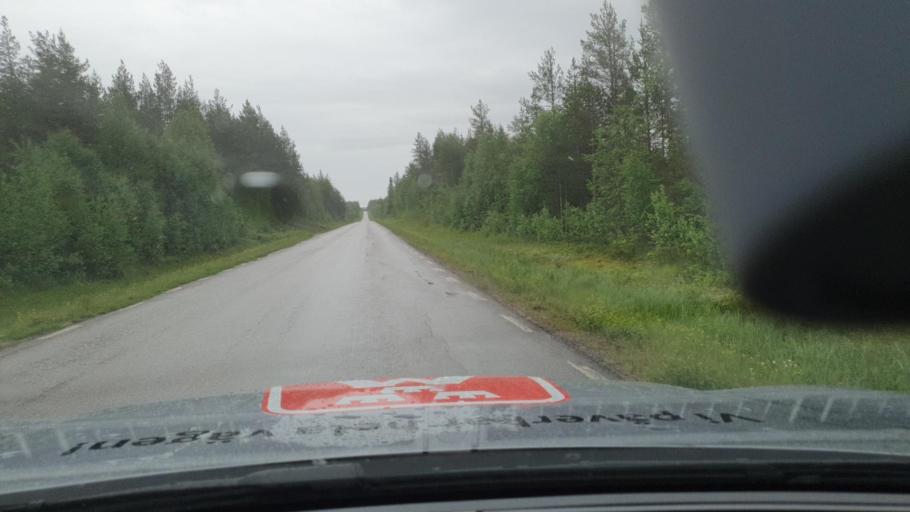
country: SE
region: Norrbotten
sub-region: Pajala Kommun
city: Pajala
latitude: 66.8373
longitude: 23.0912
